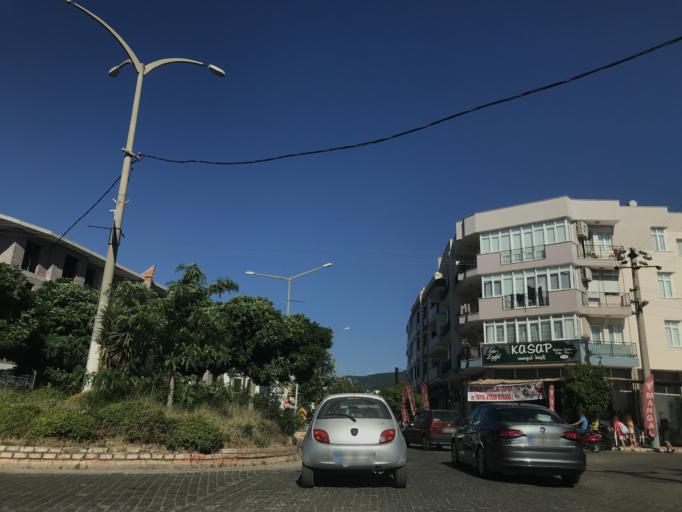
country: TR
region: Aydin
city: Davutlar
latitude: 37.7335
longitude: 27.2842
